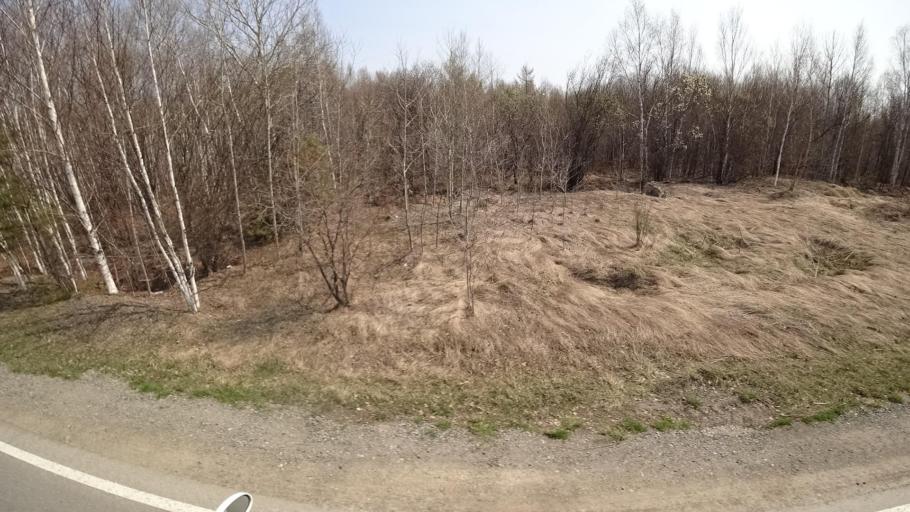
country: RU
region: Khabarovsk Krai
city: Selikhino
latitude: 50.3926
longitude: 137.3743
